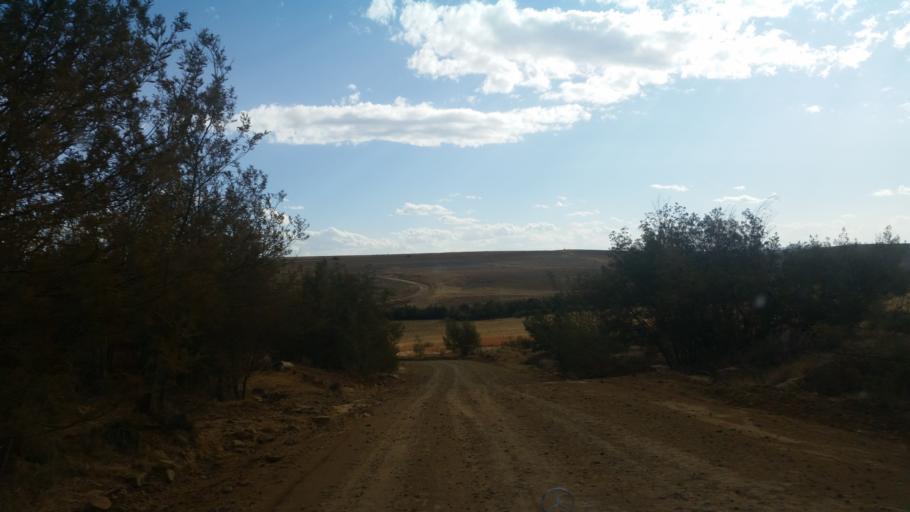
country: ZA
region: Orange Free State
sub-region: Thabo Mofutsanyana District Municipality
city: Phuthaditjhaba
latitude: -28.3484
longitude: 28.6118
